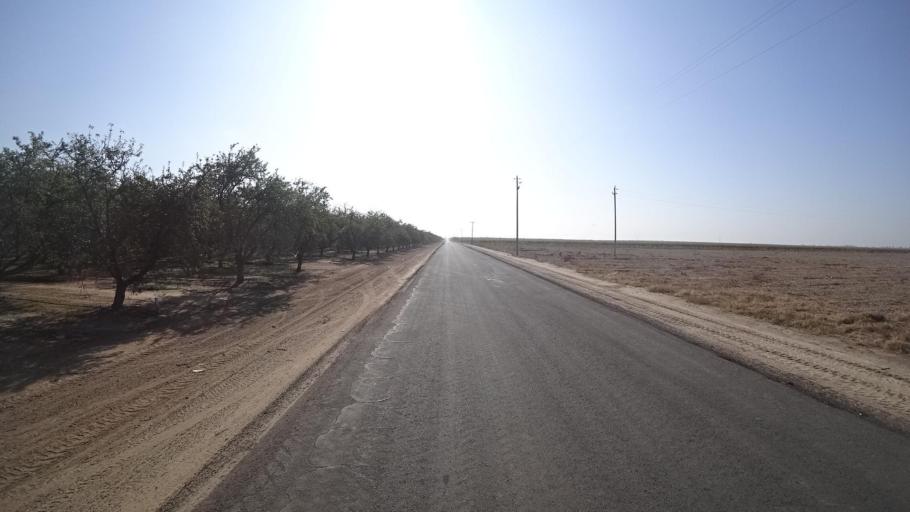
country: US
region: California
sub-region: Kern County
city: McFarland
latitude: 35.6503
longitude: -119.1867
